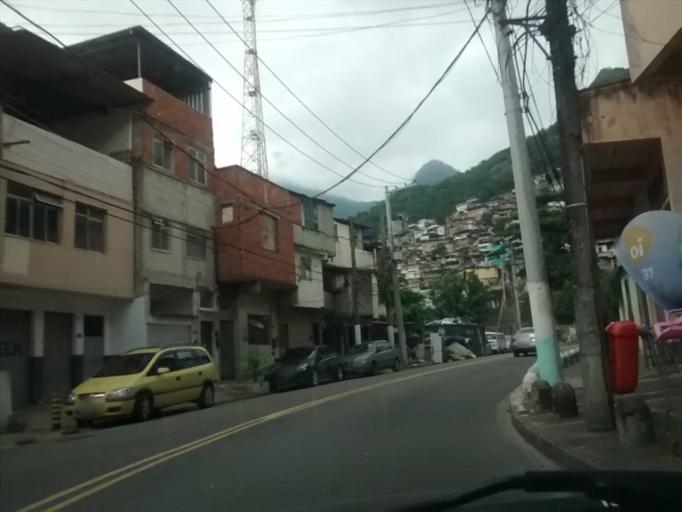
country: BR
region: Rio de Janeiro
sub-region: Rio De Janeiro
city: Rio de Janeiro
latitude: -22.9394
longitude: -43.2513
